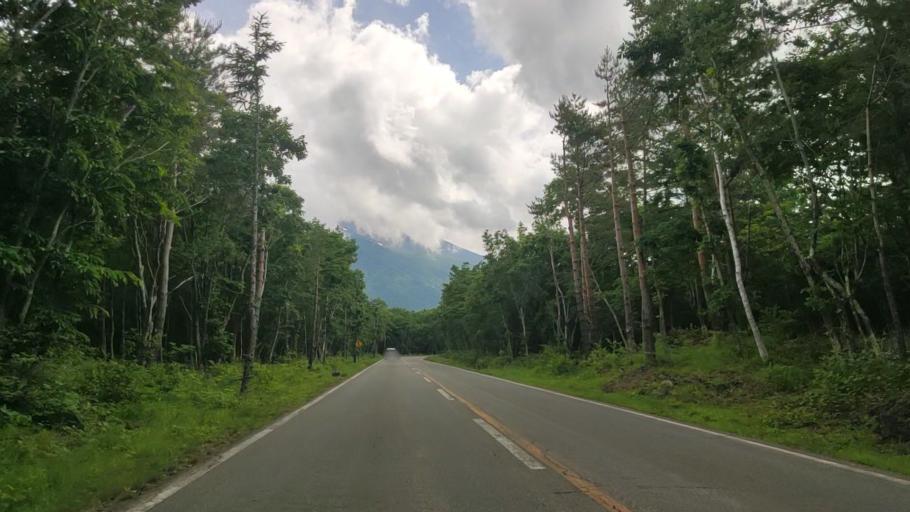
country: JP
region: Yamanashi
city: Fujikawaguchiko
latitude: 35.4403
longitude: 138.7456
